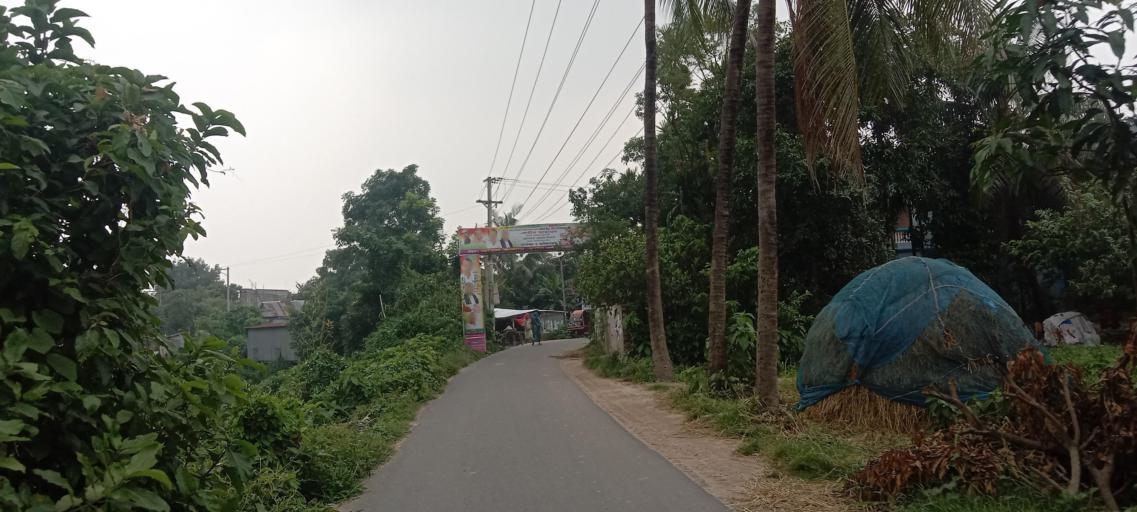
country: BD
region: Dhaka
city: Azimpur
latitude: 23.7399
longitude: 90.3136
